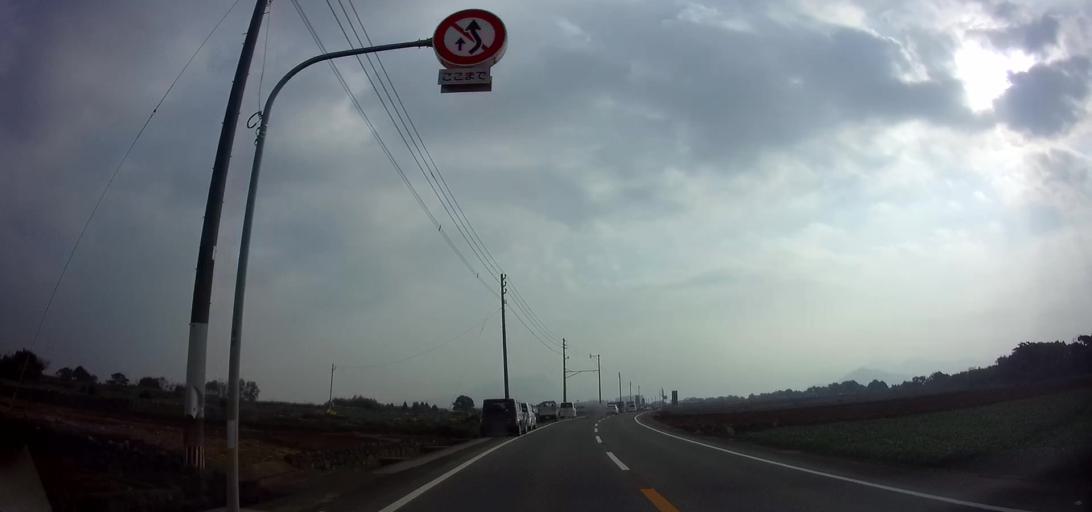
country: JP
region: Nagasaki
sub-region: Isahaya-shi
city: Isahaya
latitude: 32.7980
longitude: 130.1498
